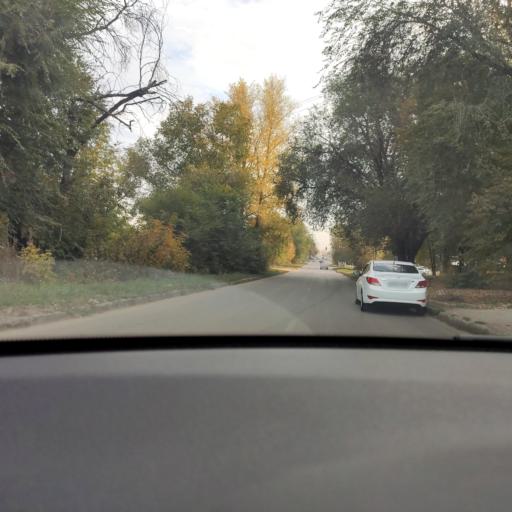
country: RU
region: Samara
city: Petra-Dubrava
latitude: 53.2487
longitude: 50.2654
